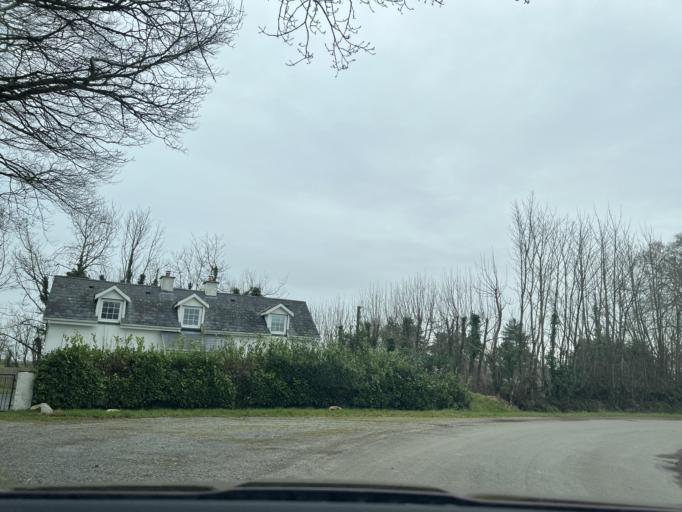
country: IE
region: Leinster
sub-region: Loch Garman
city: Castlebridge
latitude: 52.3865
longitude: -6.5266
